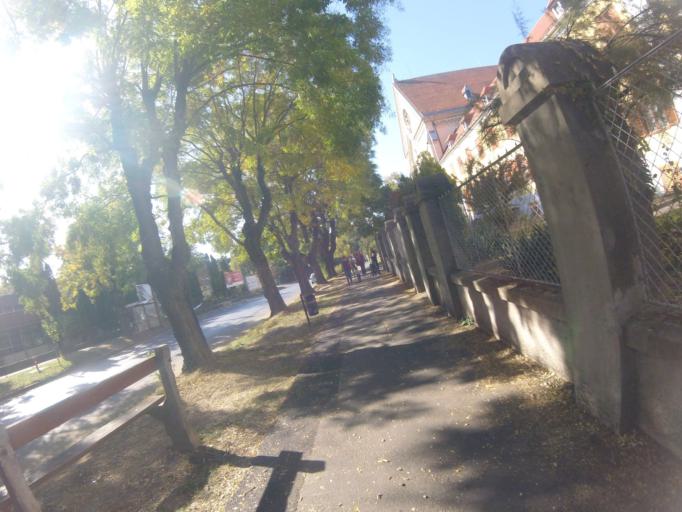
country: HU
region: Zala
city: Keszthely
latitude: 46.7701
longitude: 17.2524
